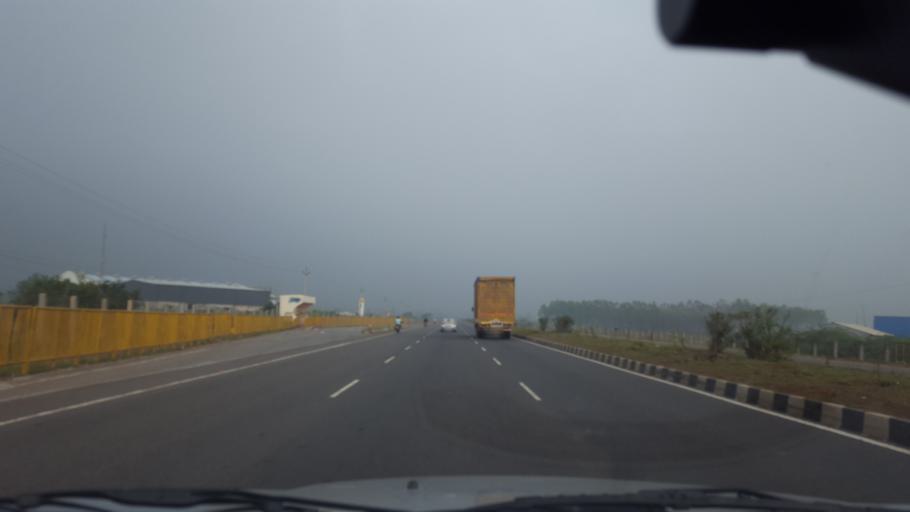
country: IN
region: Andhra Pradesh
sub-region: Prakasam
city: Ongole
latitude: 15.5766
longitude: 80.0428
